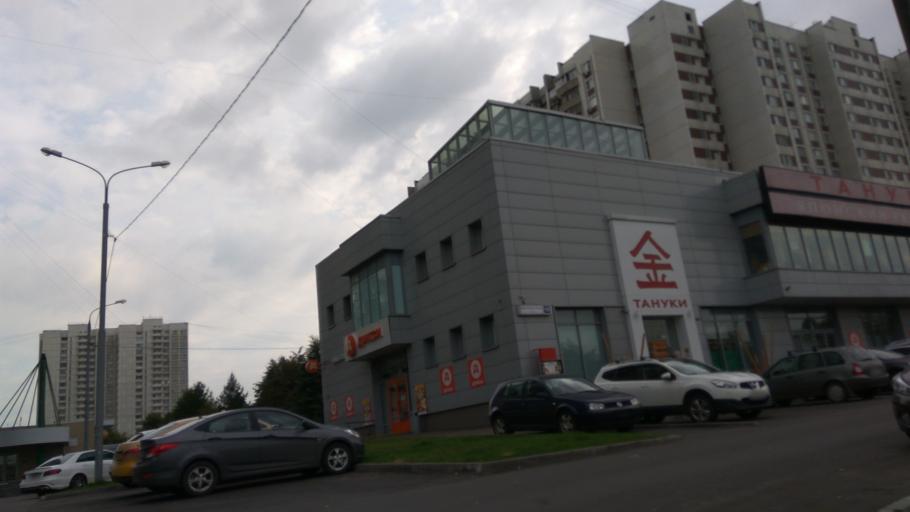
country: RU
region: Moscow
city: Brateyevo
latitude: 55.6362
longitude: 37.7413
